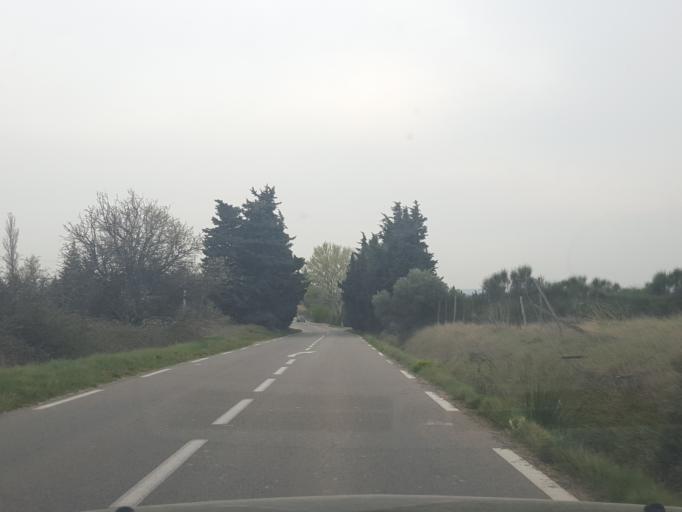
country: FR
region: Provence-Alpes-Cote d'Azur
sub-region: Departement du Vaucluse
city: Saint-Saturnin-les-Avignon
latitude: 43.9504
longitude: 4.9136
